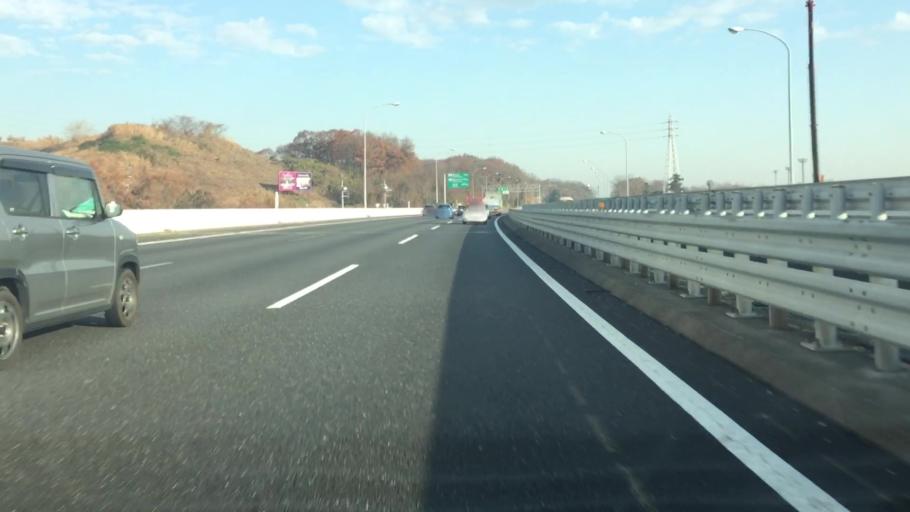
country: JP
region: Saitama
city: Sakado
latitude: 35.9808
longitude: 139.3802
